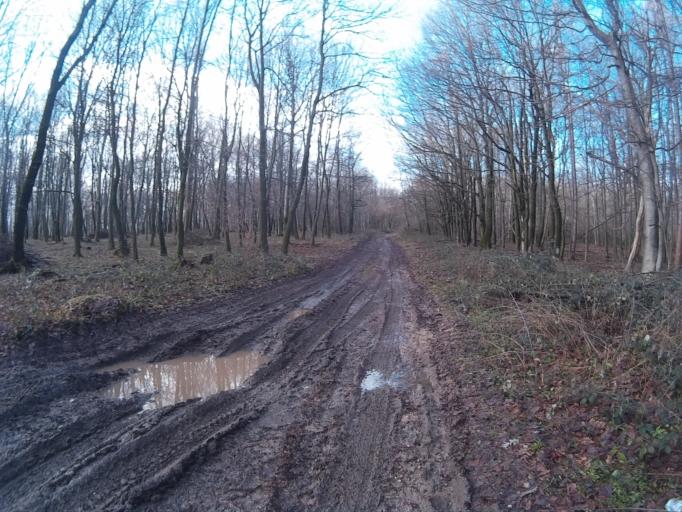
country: HU
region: Veszprem
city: Urkut
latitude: 47.1185
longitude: 17.6828
